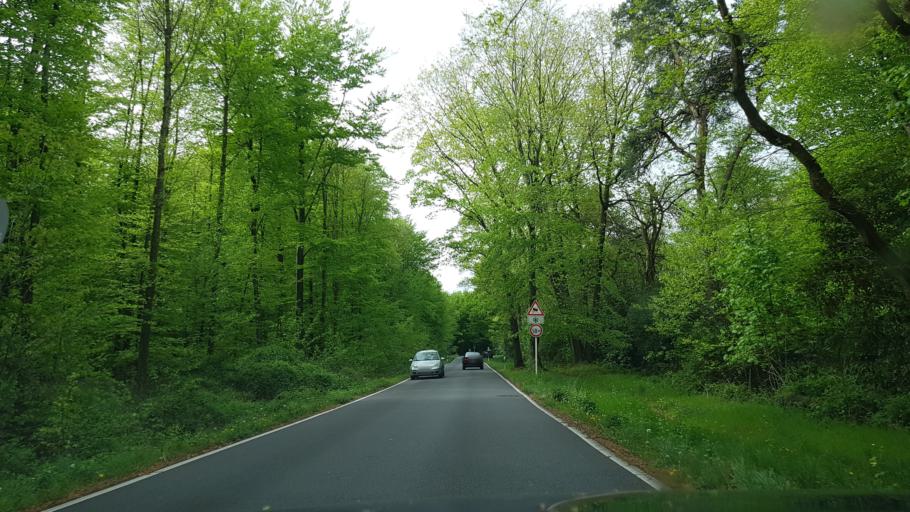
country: DE
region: North Rhine-Westphalia
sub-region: Regierungsbezirk Dusseldorf
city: Muelheim (Ruhr)
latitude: 51.3869
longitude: 6.8339
